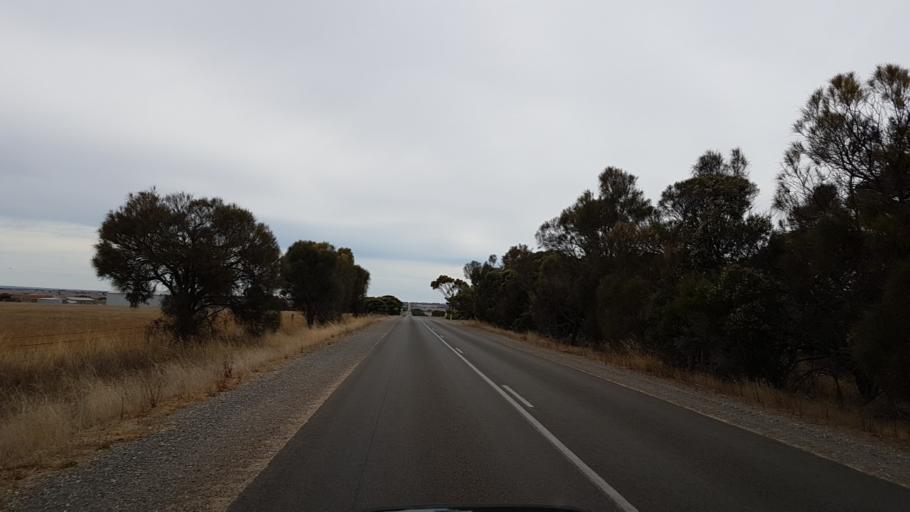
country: AU
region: South Australia
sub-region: Yorke Peninsula
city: Honiton
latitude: -34.9850
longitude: 137.3099
